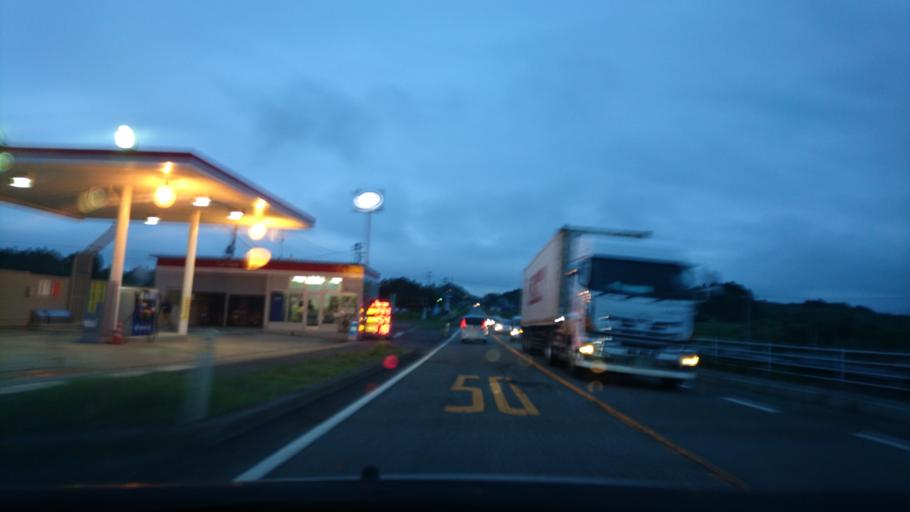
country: JP
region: Iwate
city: Ichinoseki
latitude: 38.8510
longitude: 141.0964
